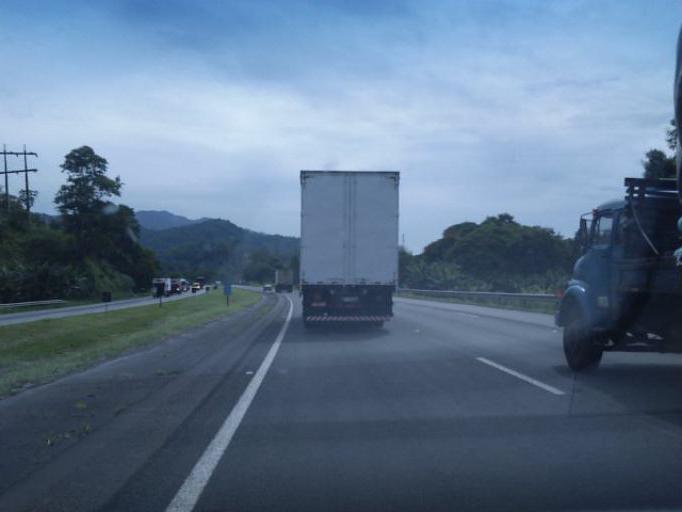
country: BR
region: Sao Paulo
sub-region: Miracatu
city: Miracatu
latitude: -24.3170
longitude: -47.5286
